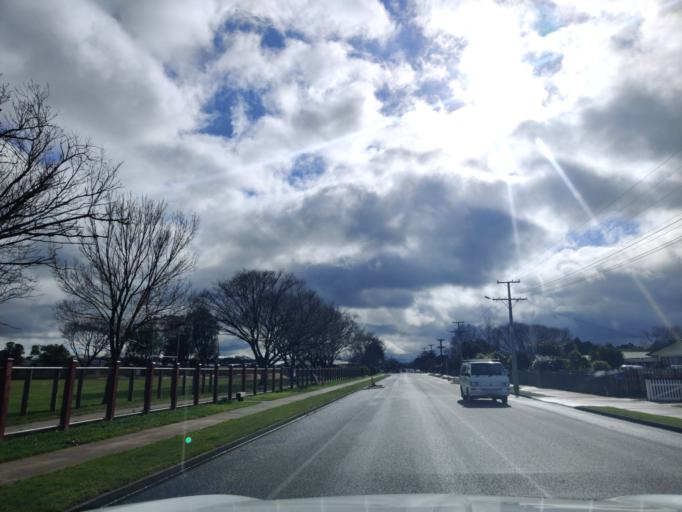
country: NZ
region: Manawatu-Wanganui
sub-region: Palmerston North City
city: Palmerston North
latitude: -40.2908
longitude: 175.7577
